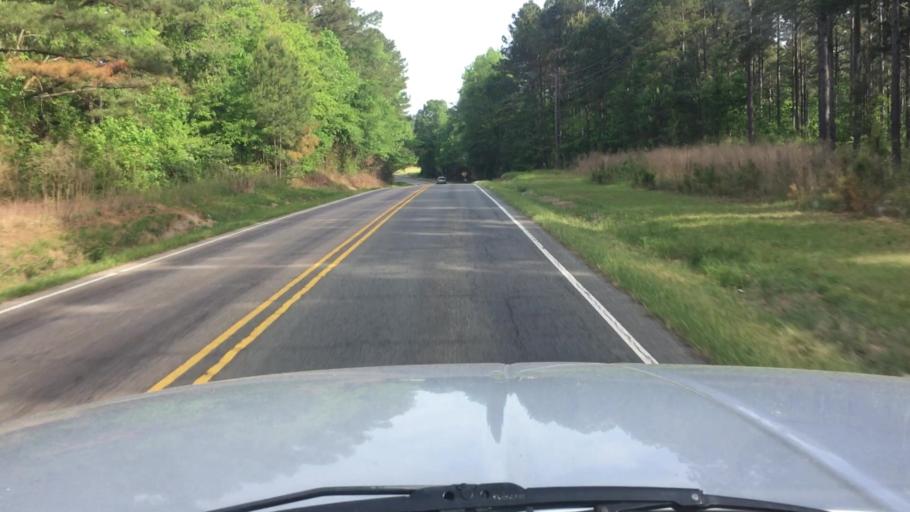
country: US
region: North Carolina
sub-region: Johnston County
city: Wilsons Mills
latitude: 35.6337
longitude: -78.3323
